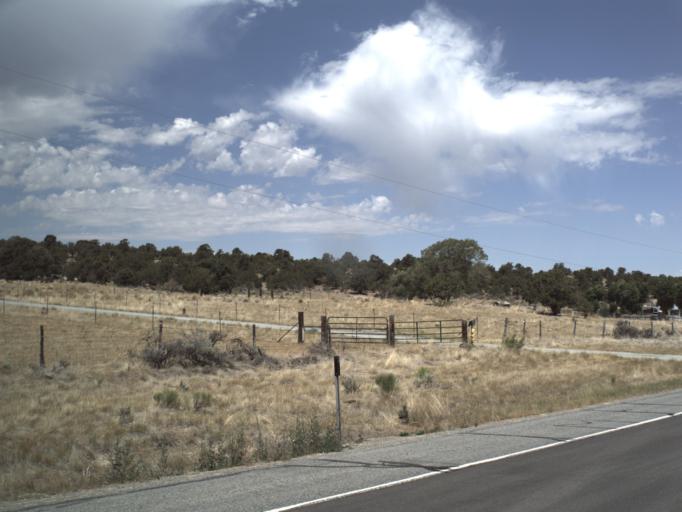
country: US
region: Utah
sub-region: Utah County
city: Eagle Mountain
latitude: 40.0223
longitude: -112.2807
